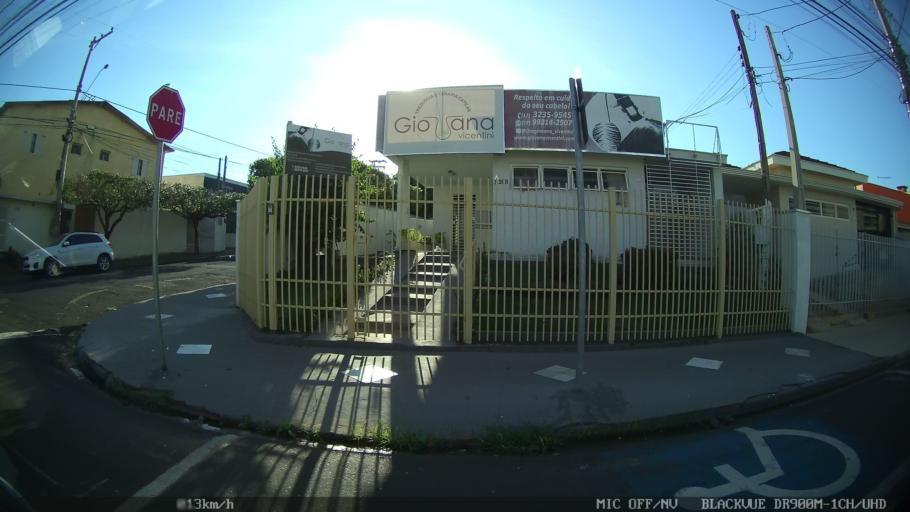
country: BR
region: Sao Paulo
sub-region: Sao Jose Do Rio Preto
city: Sao Jose do Rio Preto
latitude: -20.8154
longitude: -49.3945
